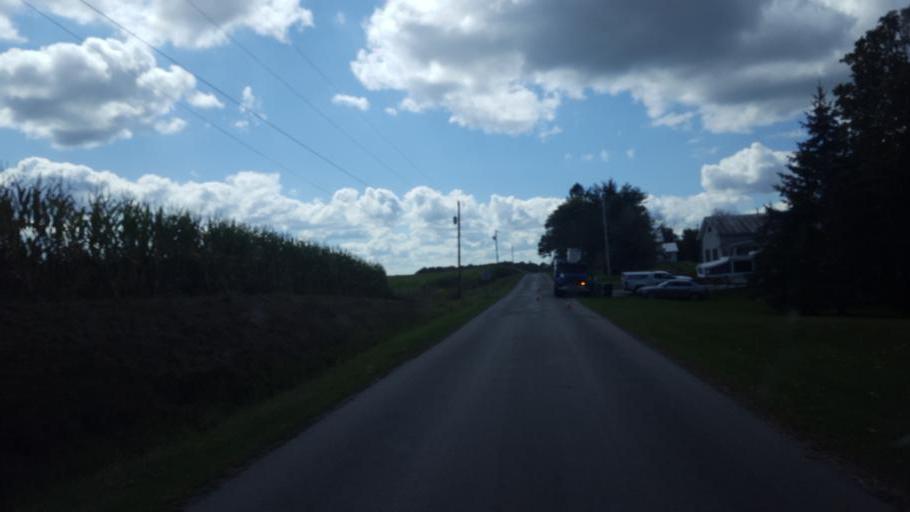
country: US
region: Ohio
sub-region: Medina County
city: Lodi
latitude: 41.0784
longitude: -82.0950
